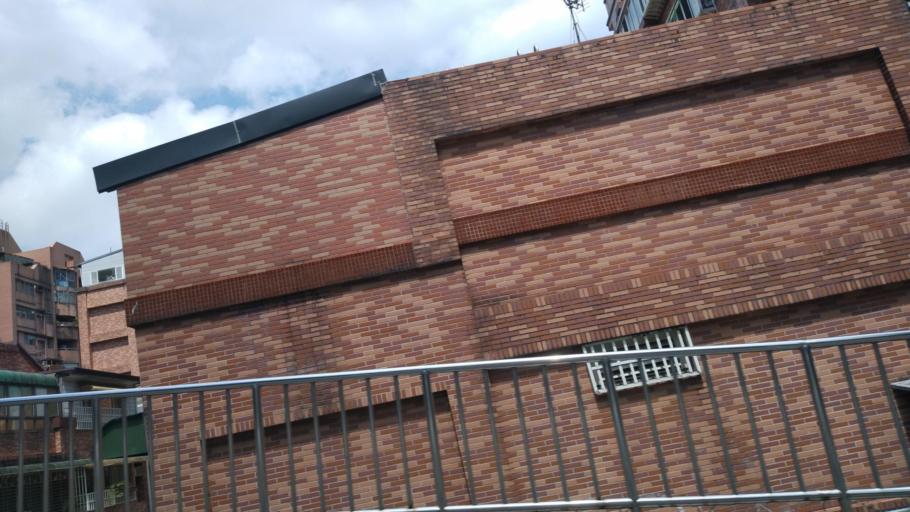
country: TW
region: Taipei
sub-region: Taipei
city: Banqiao
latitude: 24.9476
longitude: 121.4957
